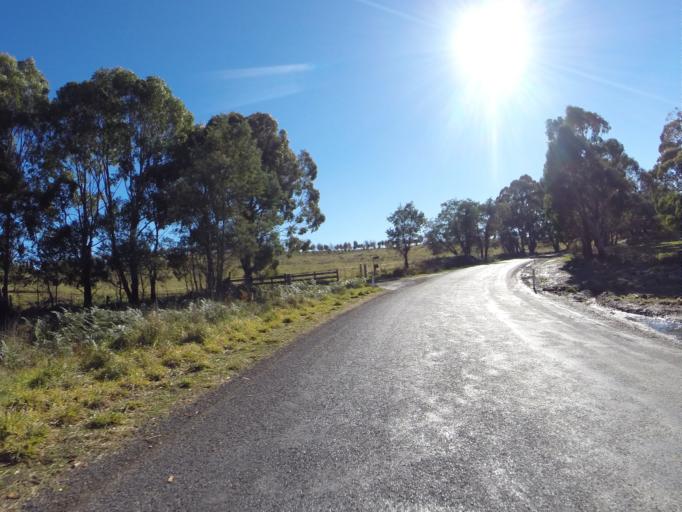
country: AU
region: New South Wales
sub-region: Oberon
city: Oberon
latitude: -33.6269
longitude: 149.8450
